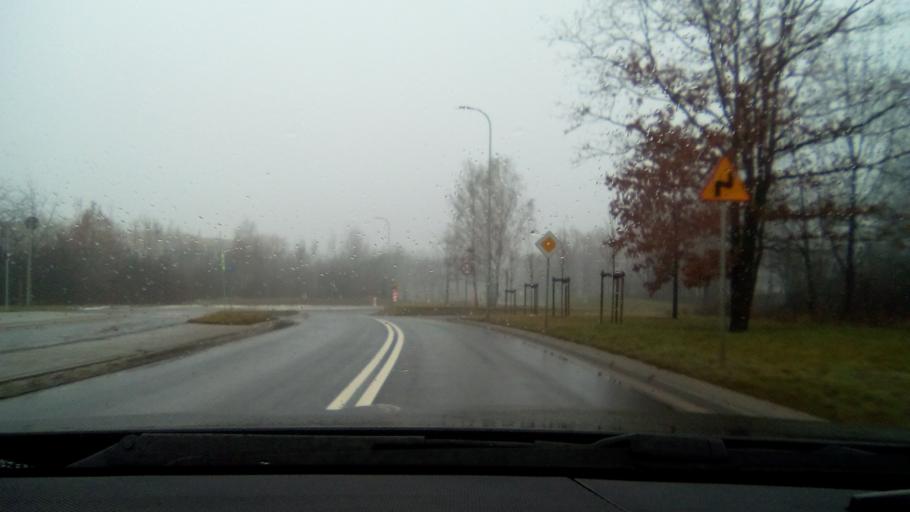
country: PL
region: Greater Poland Voivodeship
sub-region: Powiat poznanski
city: Swarzedz
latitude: 52.3870
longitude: 17.0098
